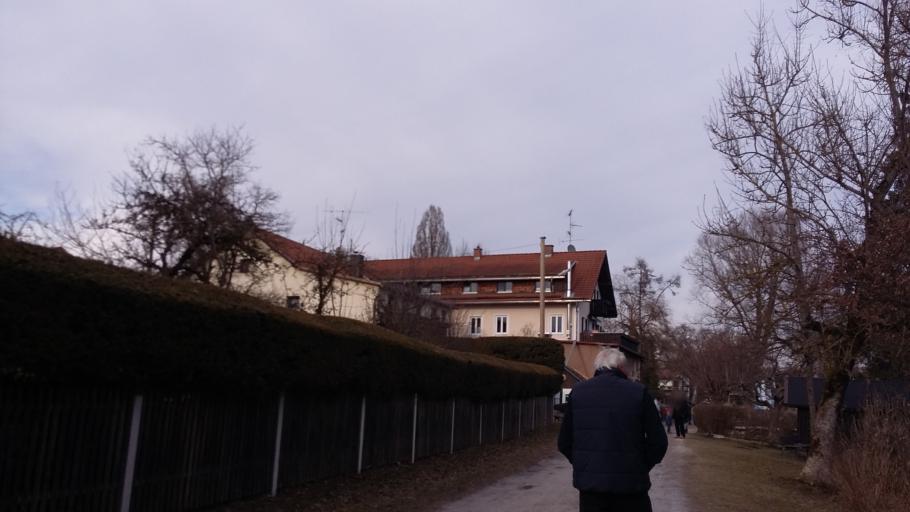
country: DE
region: Bavaria
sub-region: Upper Bavaria
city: Wessling
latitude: 48.0726
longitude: 11.2477
